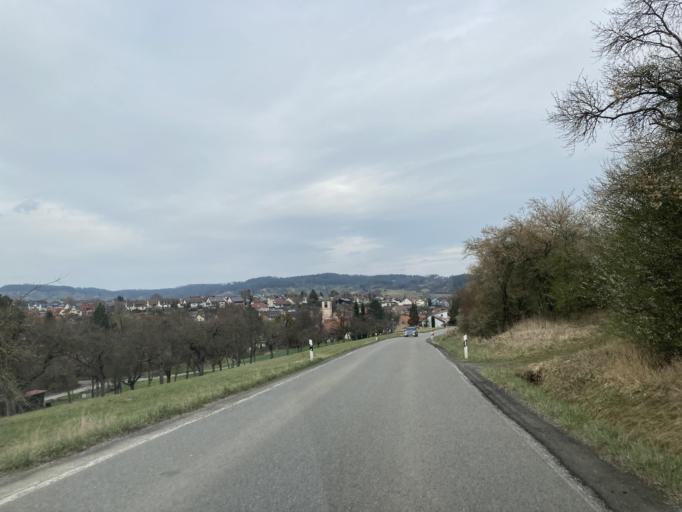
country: DE
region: Baden-Wuerttemberg
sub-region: Tuebingen Region
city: Rottenburg
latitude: 48.5326
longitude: 8.9425
